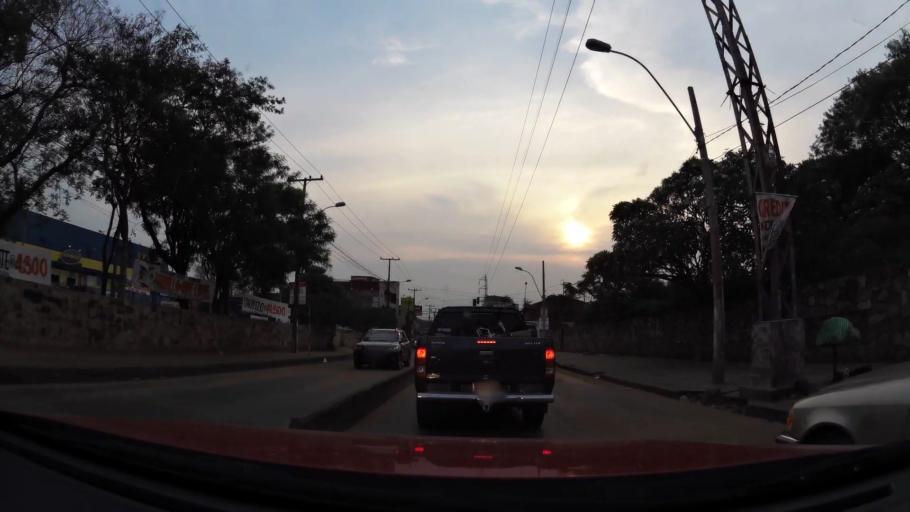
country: PY
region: Central
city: Lambare
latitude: -25.3419
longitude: -57.6041
